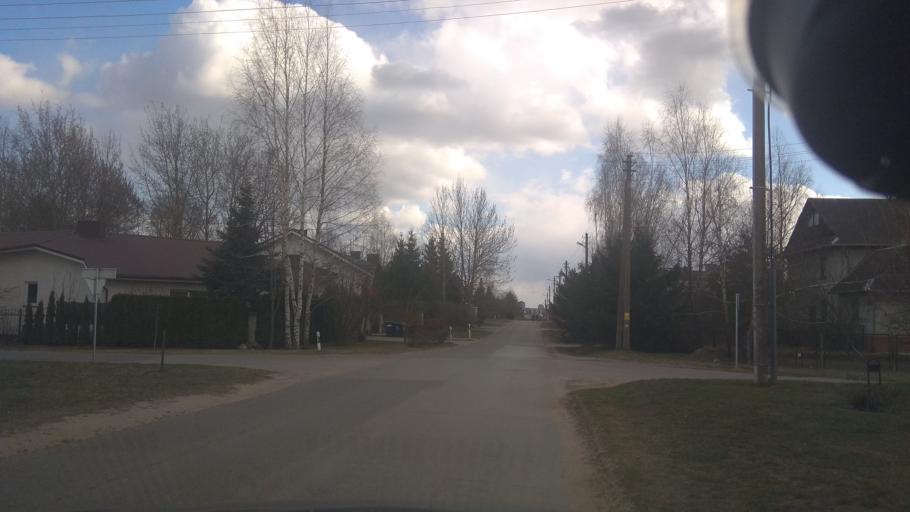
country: LT
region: Vilnius County
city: Pasilaiciai
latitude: 54.7425
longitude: 25.2005
